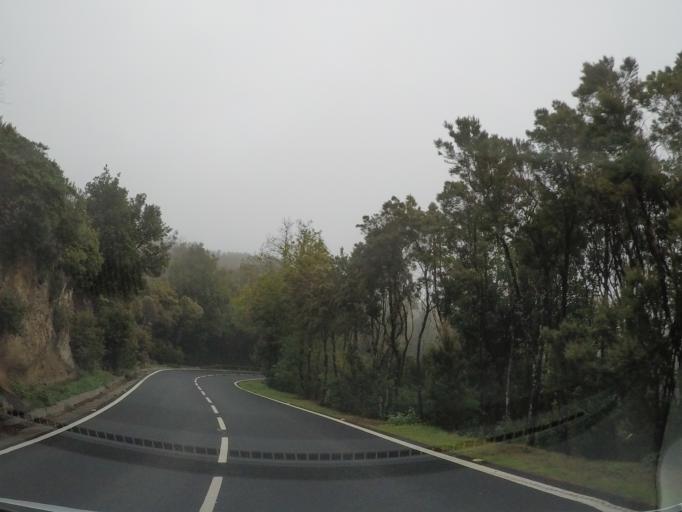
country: ES
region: Canary Islands
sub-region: Provincia de Santa Cruz de Tenerife
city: Alajero
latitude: 28.1205
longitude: -17.2497
